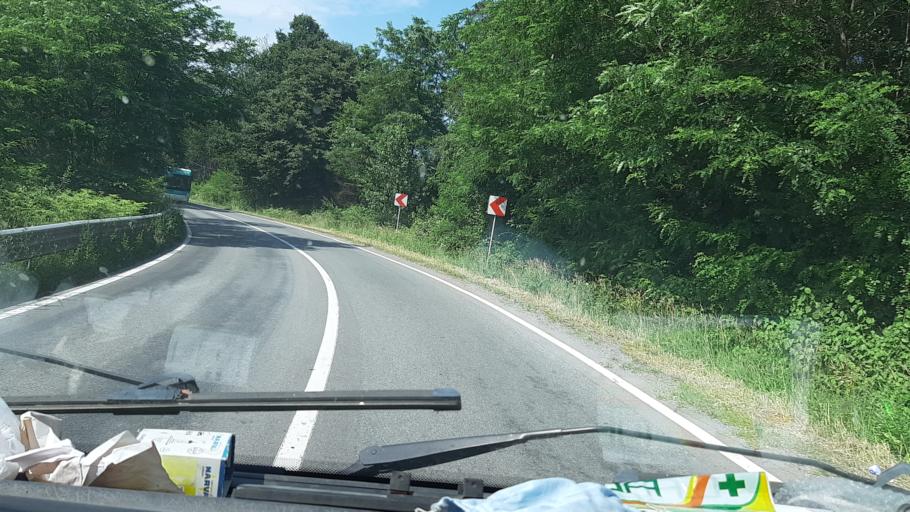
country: RO
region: Caras-Severin
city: Resita
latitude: 45.3560
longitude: 21.9286
